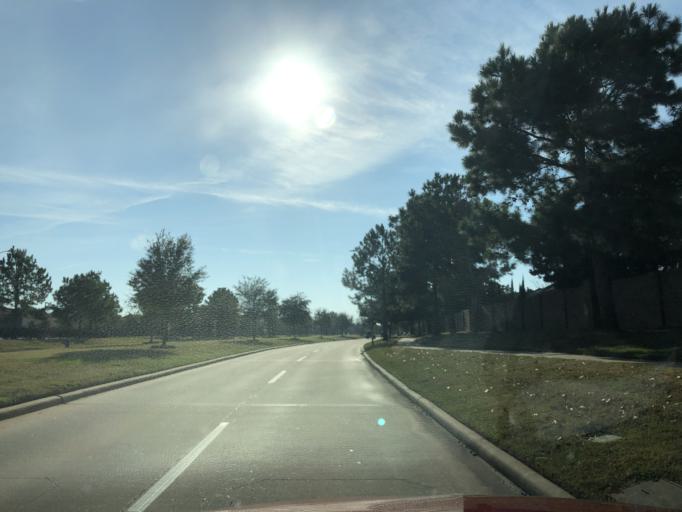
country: US
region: Texas
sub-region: Harris County
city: Tomball
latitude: 30.0532
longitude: -95.5686
